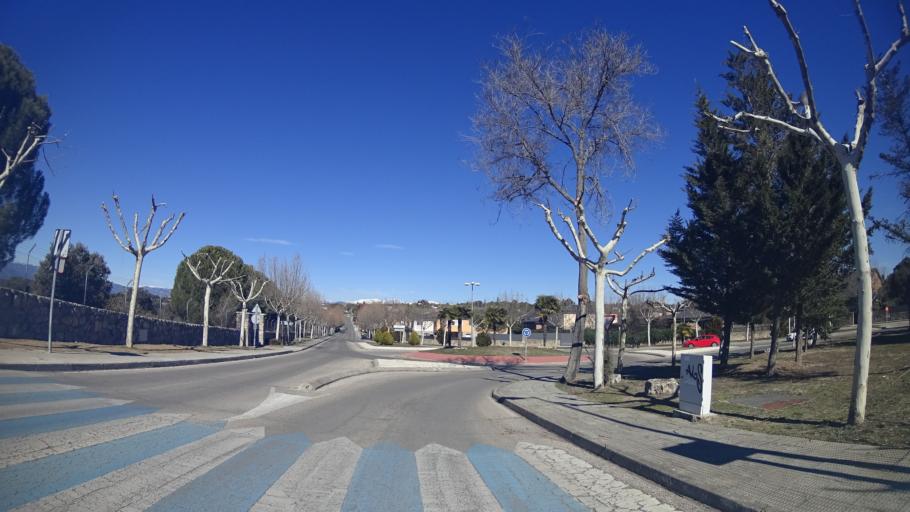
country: ES
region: Madrid
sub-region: Provincia de Madrid
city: Colmenarejo
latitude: 40.5530
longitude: -4.0133
